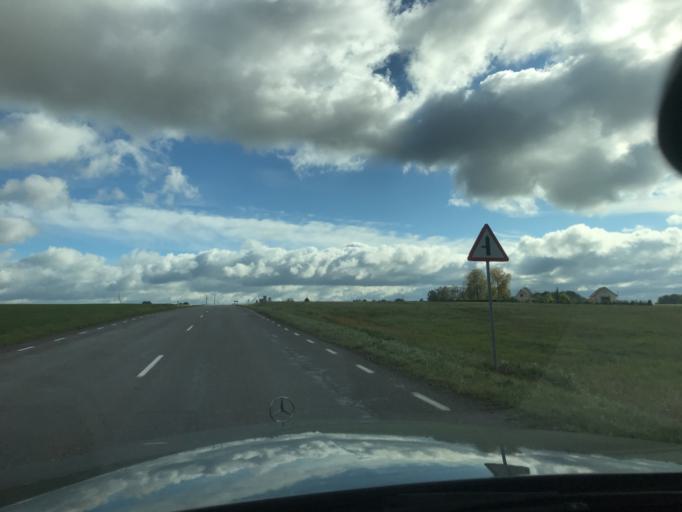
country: EE
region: Vorumaa
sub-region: Antsla vald
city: Vana-Antsla
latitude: 57.9032
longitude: 26.4659
